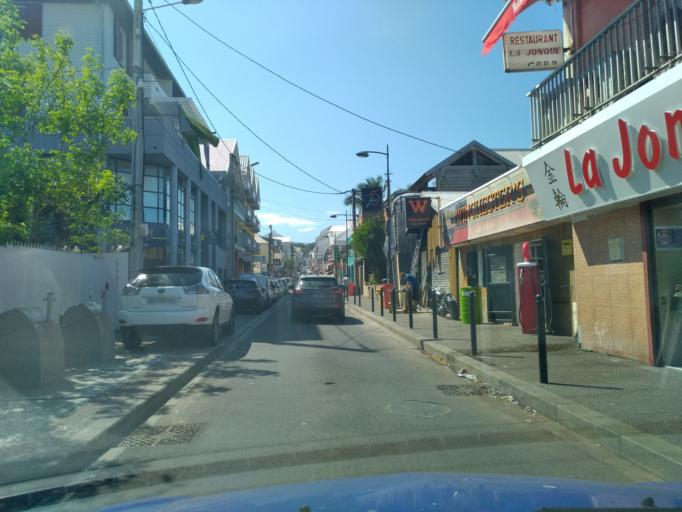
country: RE
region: Reunion
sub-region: Reunion
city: Saint-Pierre
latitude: -21.3434
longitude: 55.4744
